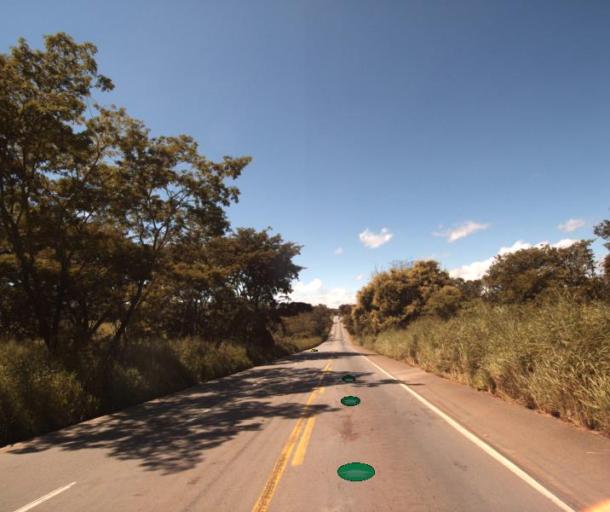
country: BR
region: Goias
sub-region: Jaragua
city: Jaragua
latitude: -15.6294
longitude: -49.3822
